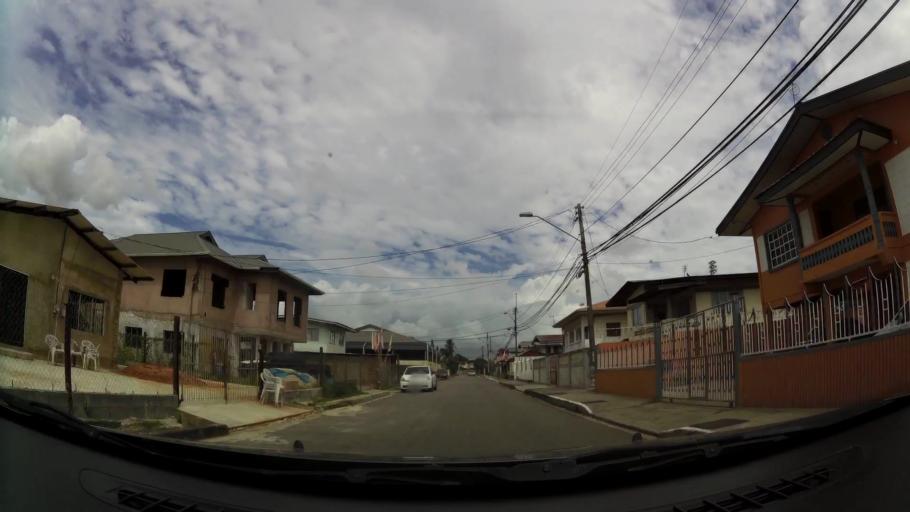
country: TT
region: Couva-Tabaquite-Talparo
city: Couva
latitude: 10.3993
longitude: -61.4712
